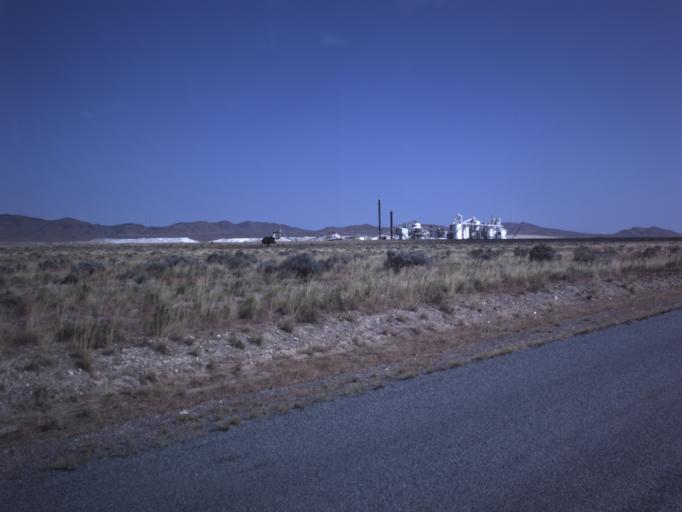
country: US
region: Utah
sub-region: Millard County
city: Delta
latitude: 38.9272
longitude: -112.8106
